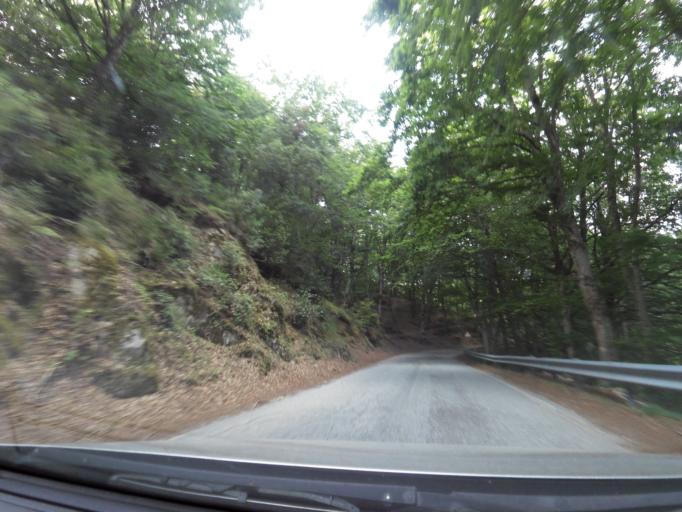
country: IT
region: Calabria
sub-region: Provincia di Vibo-Valentia
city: Nardodipace
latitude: 38.4823
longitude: 16.3791
